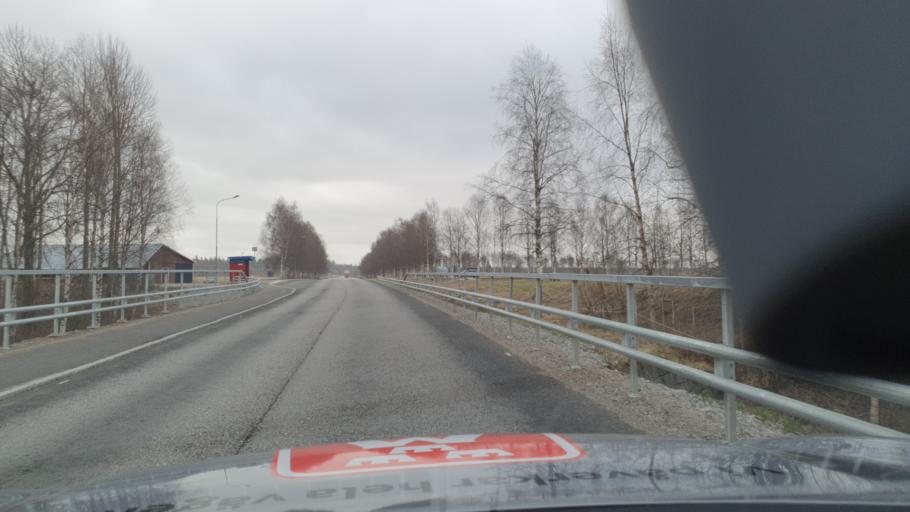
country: SE
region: Norrbotten
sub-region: Kalix Kommun
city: Rolfs
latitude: 65.8813
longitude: 23.0710
